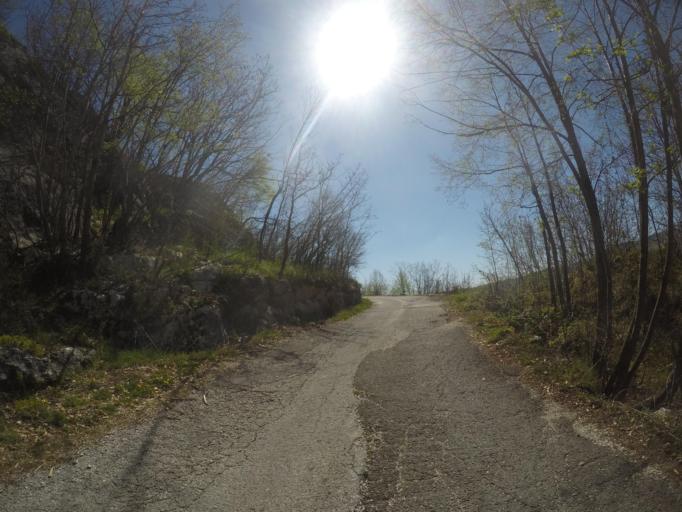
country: ME
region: Cetinje
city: Cetinje
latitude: 42.5280
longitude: 18.9516
